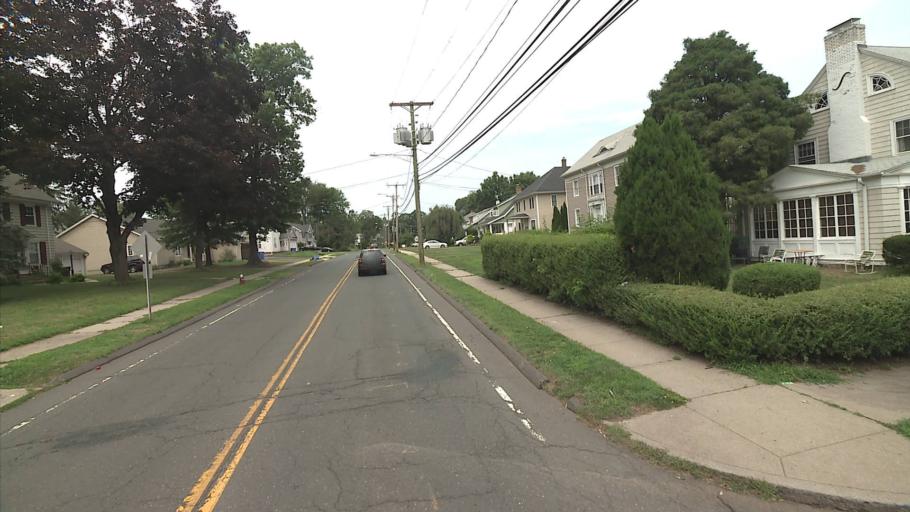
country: US
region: Connecticut
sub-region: Hartford County
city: New Britain
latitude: 41.6861
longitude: -72.7688
